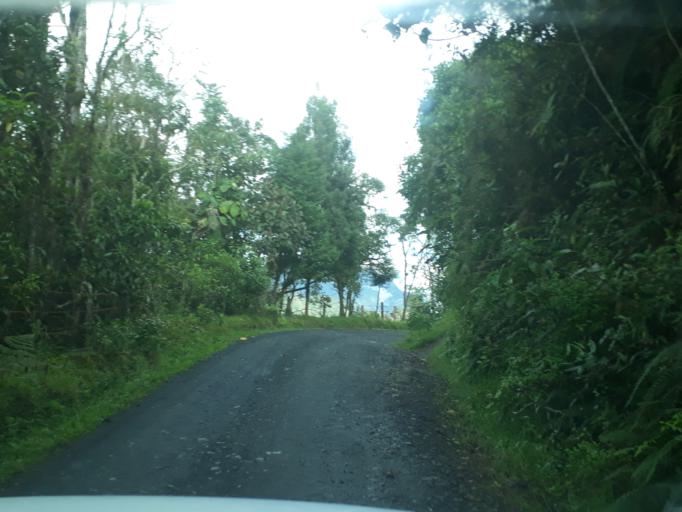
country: CO
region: Cundinamarca
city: La Mesa
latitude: 5.3303
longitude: -74.0543
